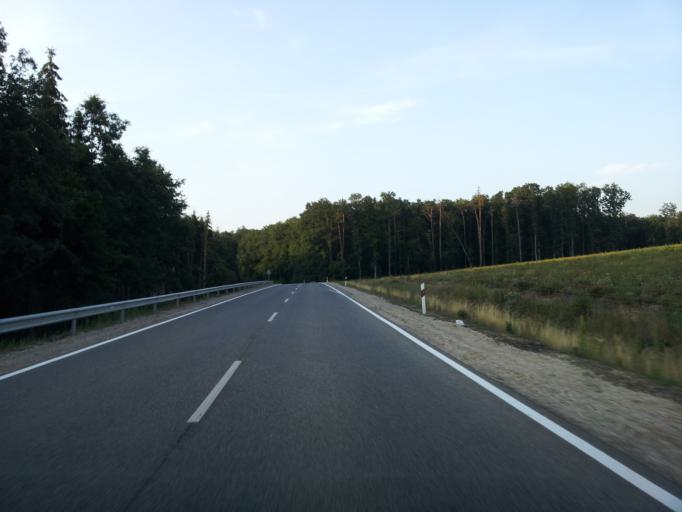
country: HU
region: Zala
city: Zalalovo
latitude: 46.7846
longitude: 16.5668
